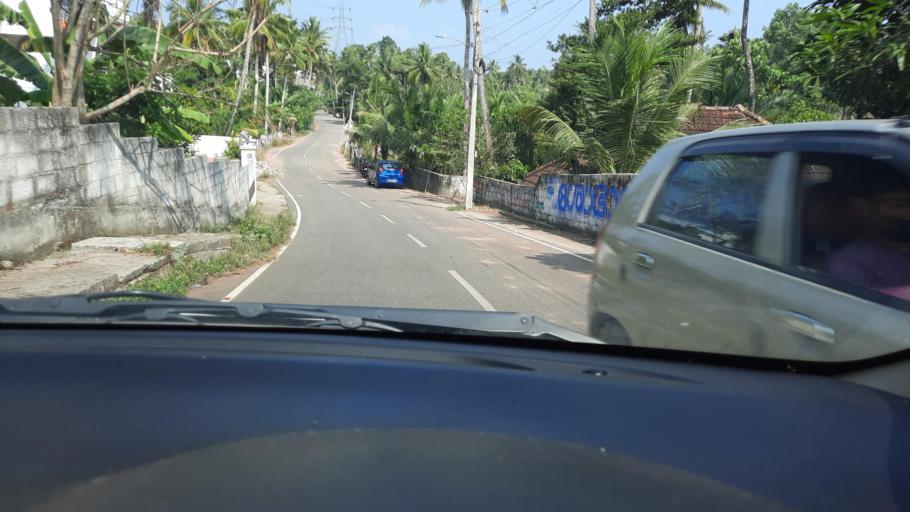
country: IN
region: Kerala
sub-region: Thiruvananthapuram
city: Nedumangad
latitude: 8.5857
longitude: 76.9226
